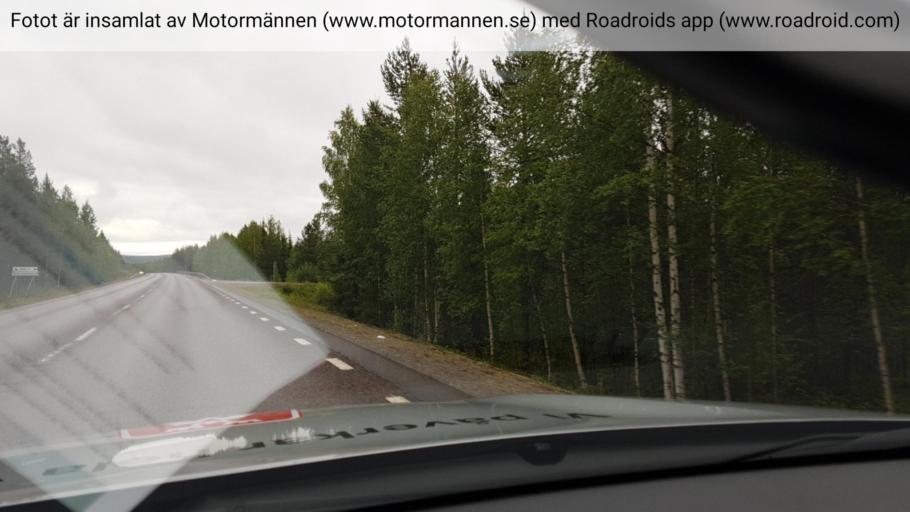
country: SE
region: Norrbotten
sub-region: Gallivare Kommun
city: Gaellivare
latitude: 67.1201
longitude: 20.7640
